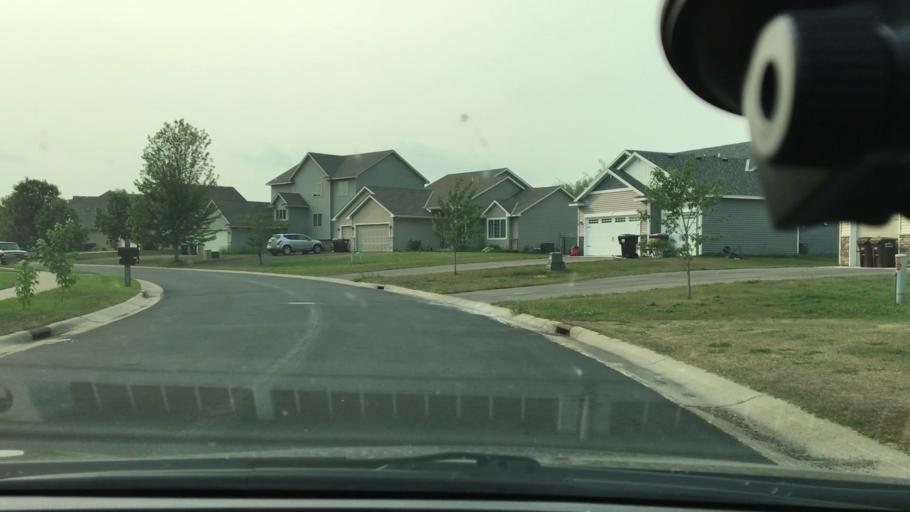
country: US
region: Minnesota
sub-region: Wright County
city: Albertville
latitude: 45.2547
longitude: -93.6549
